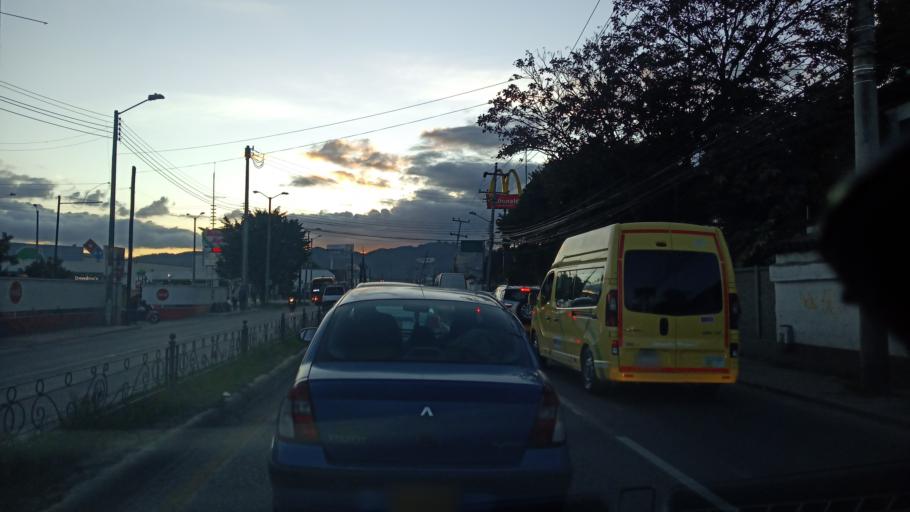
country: CO
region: Cundinamarca
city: Chia
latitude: 4.8644
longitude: -74.0419
